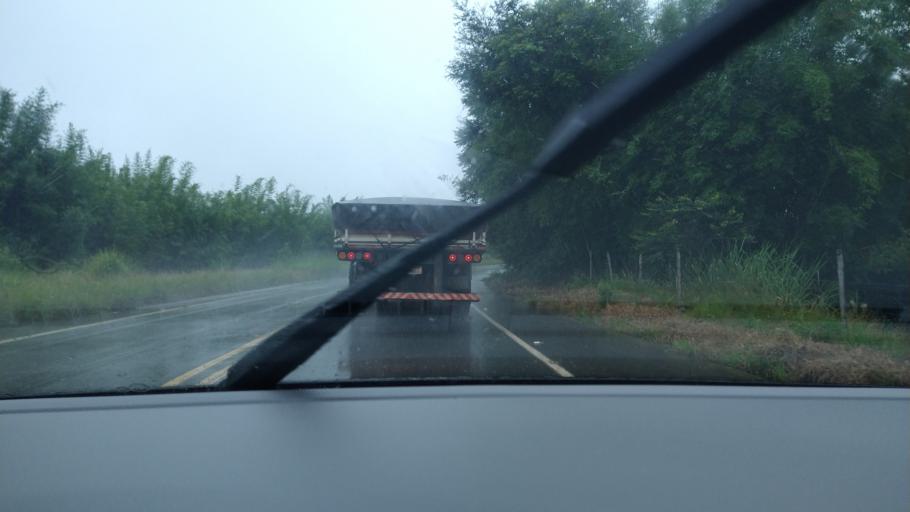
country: BR
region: Minas Gerais
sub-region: Ponte Nova
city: Ponte Nova
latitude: -20.5740
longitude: -42.8753
